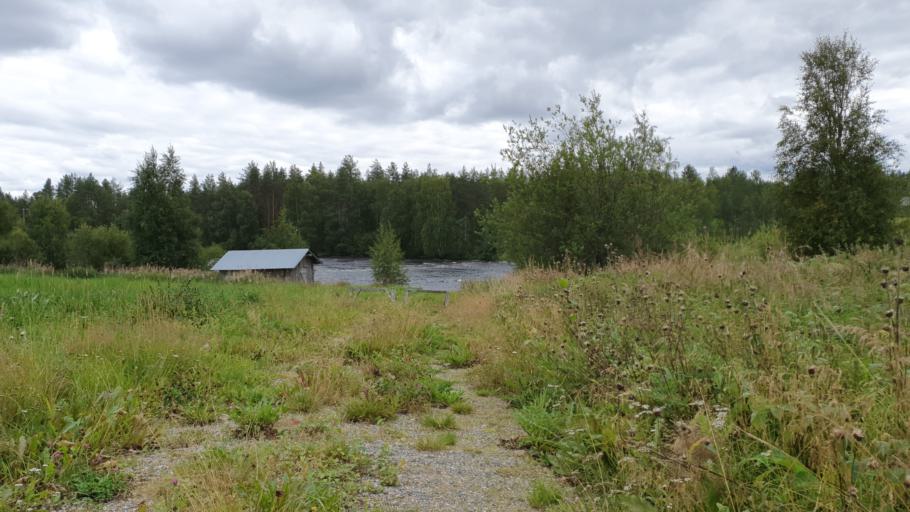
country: FI
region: Kainuu
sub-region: Kehys-Kainuu
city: Kuhmo
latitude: 64.1246
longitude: 29.4586
